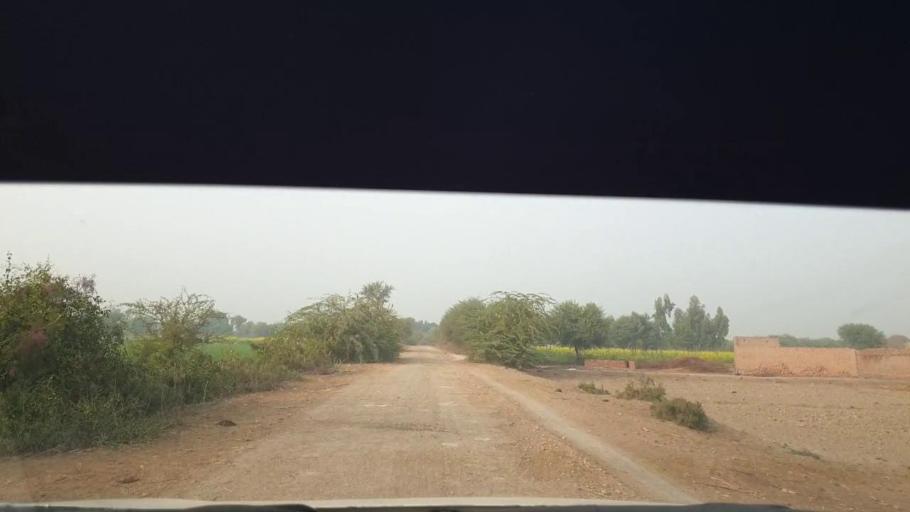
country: PK
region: Sindh
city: Berani
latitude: 25.8291
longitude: 68.8914
